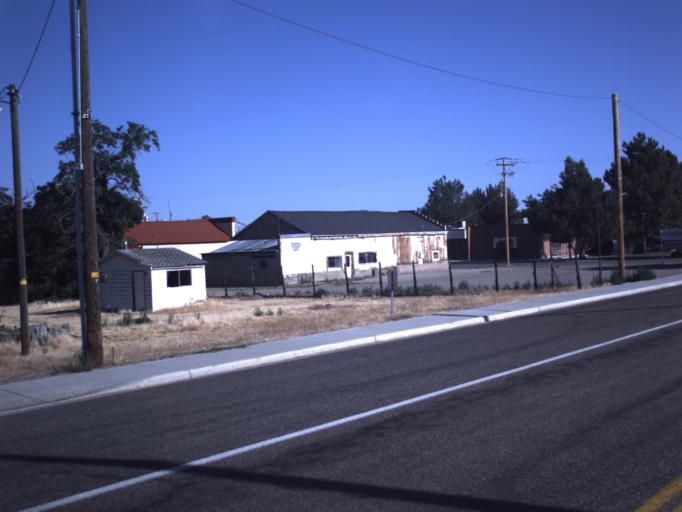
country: US
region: Utah
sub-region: Beaver County
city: Milford
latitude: 38.2147
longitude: -112.9239
